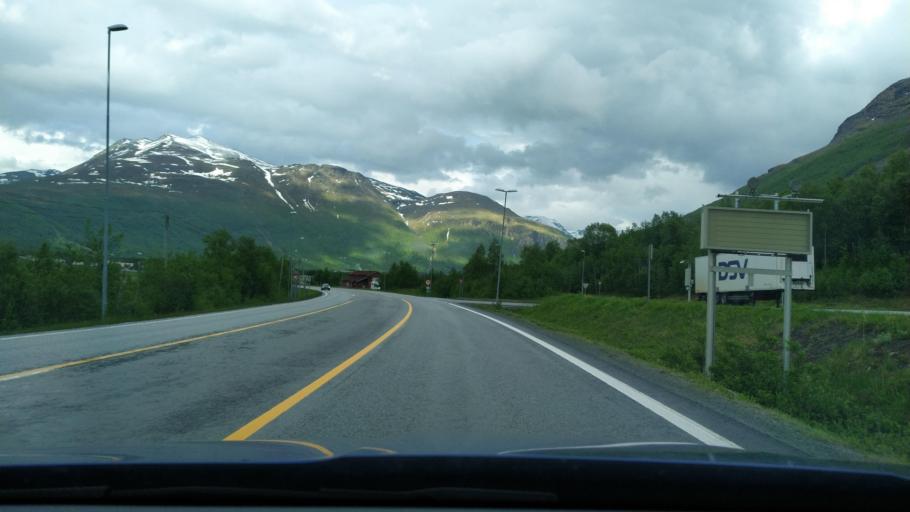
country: NO
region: Troms
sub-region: Balsfjord
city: Storsteinnes
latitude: 69.2131
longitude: 19.5339
